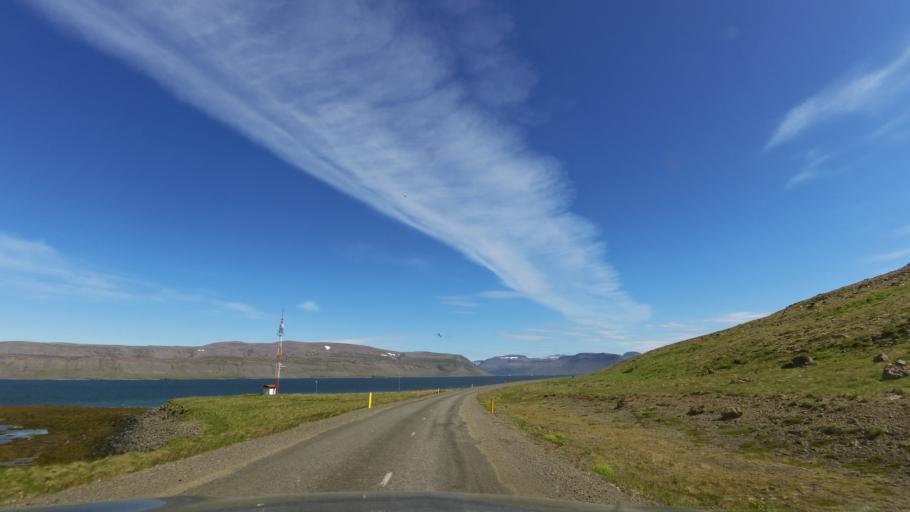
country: IS
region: Westfjords
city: Isafjoerdur
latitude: 65.6814
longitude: -23.5796
